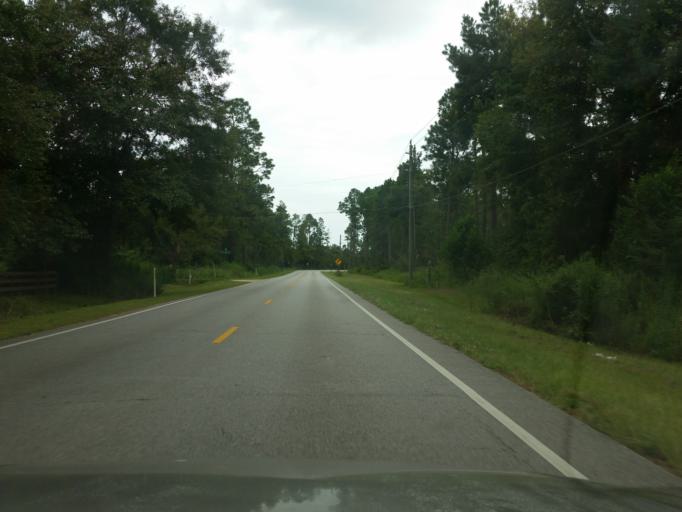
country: US
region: Florida
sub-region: Escambia County
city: Molino
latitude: 30.6802
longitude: -87.3208
